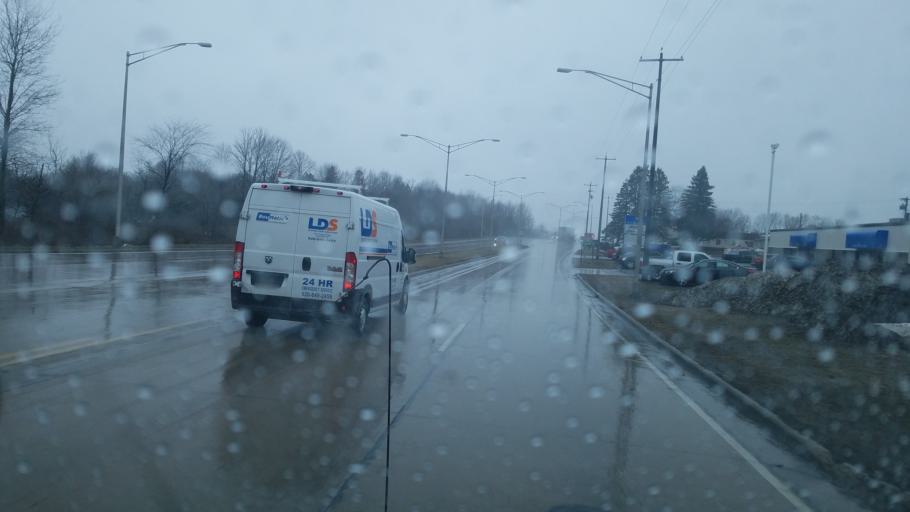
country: US
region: Wisconsin
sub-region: Wood County
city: Marshfield
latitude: 44.6742
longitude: -90.1874
